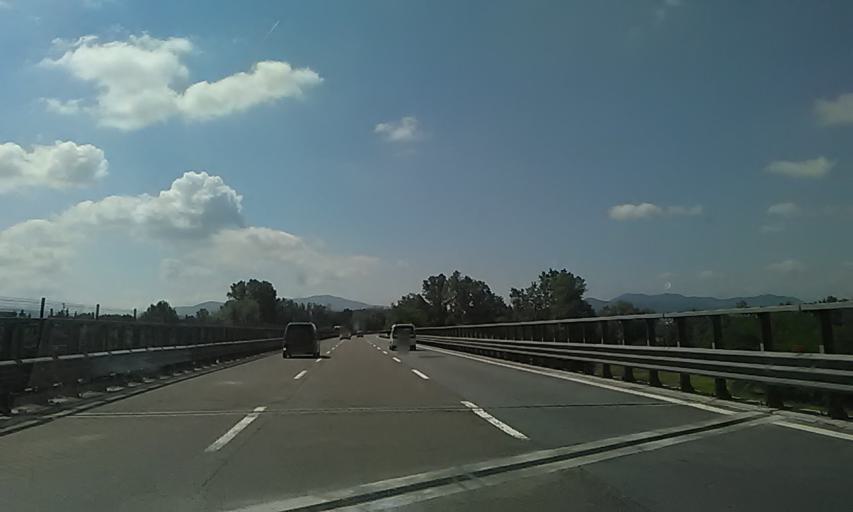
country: IT
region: Piedmont
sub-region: Provincia di Alessandria
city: Rocca Grimalda
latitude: 44.6727
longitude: 8.6589
